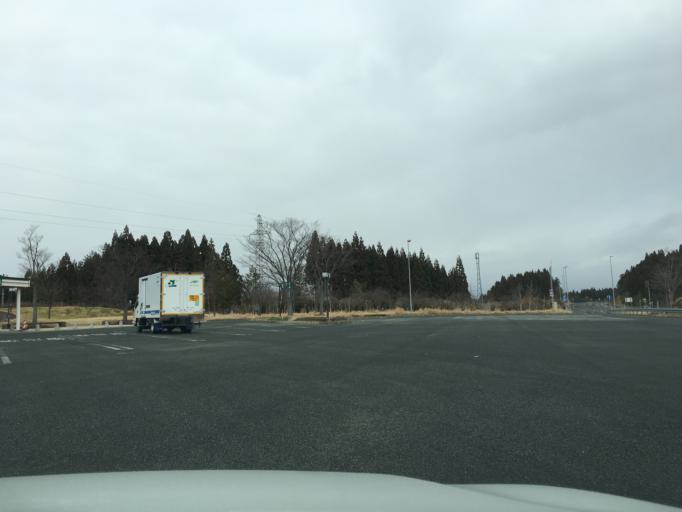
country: JP
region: Akita
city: Tenno
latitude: 40.0093
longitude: 140.0867
